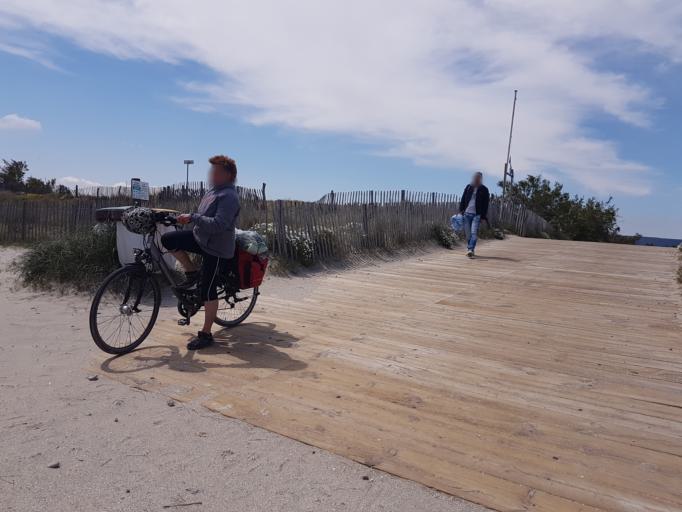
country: FR
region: Languedoc-Roussillon
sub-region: Departement de l'Herault
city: Vic-la-Gardiole
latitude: 43.4539
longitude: 3.8126
